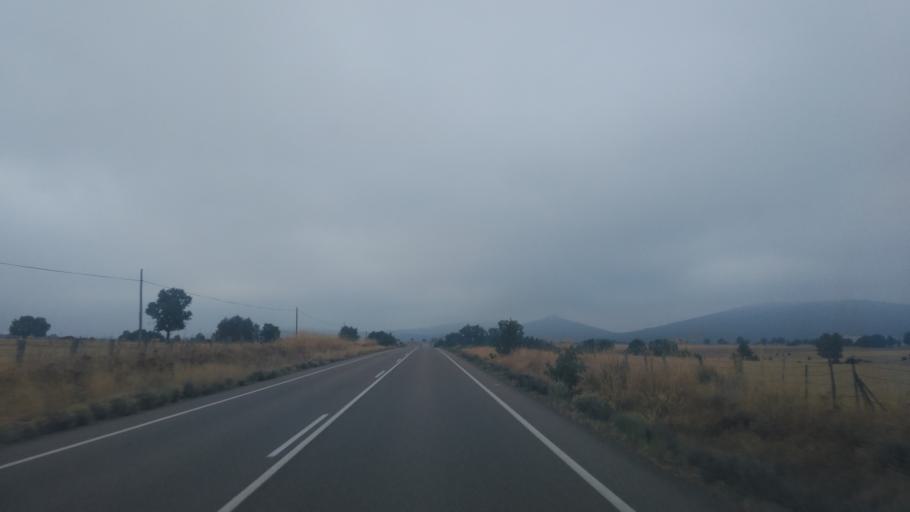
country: ES
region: Castille and Leon
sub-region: Provincia de Salamanca
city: Aldeanueva de la Sierra
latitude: 40.6357
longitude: -6.1104
